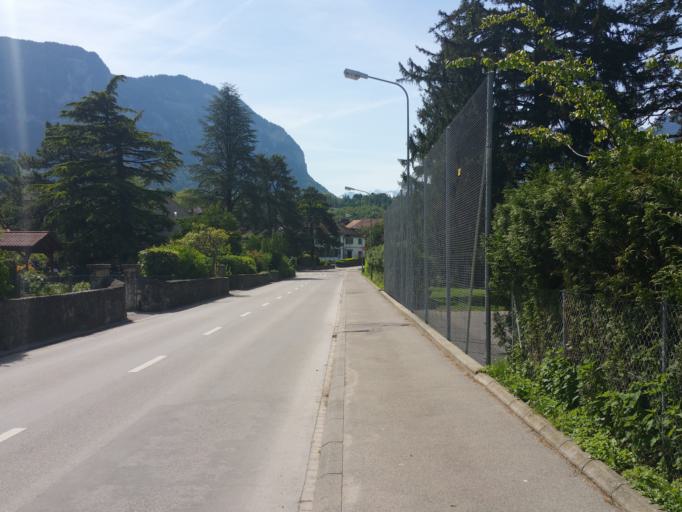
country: CH
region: Vaud
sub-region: Aigle District
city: Bex
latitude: 46.2488
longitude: 7.0124
